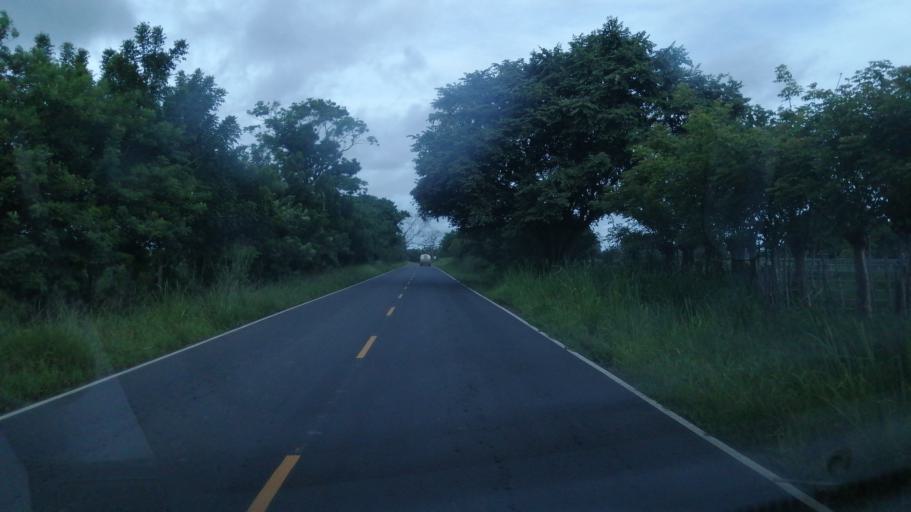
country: PA
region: Chiriqui
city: Alanje
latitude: 8.4093
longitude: -82.5151
